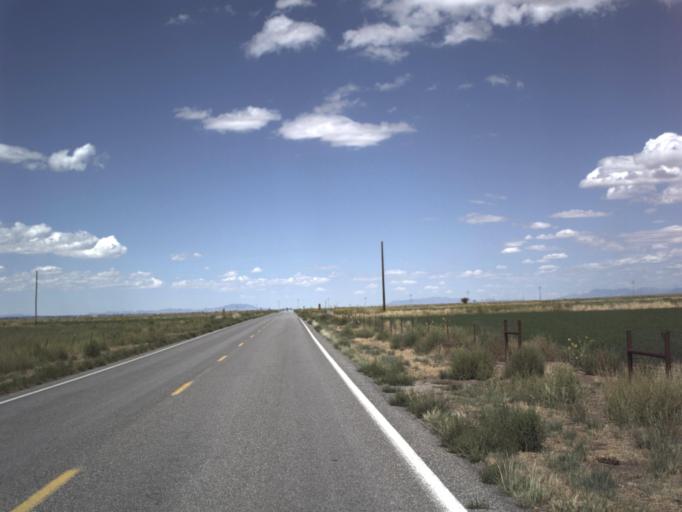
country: US
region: Utah
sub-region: Millard County
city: Delta
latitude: 39.2110
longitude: -112.4146
